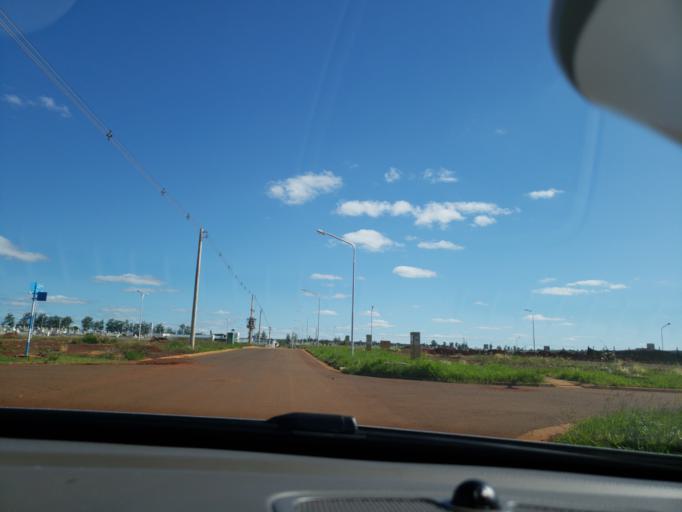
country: AR
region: Misiones
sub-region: Departamento de Capital
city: Posadas
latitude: -27.4059
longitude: -55.9837
